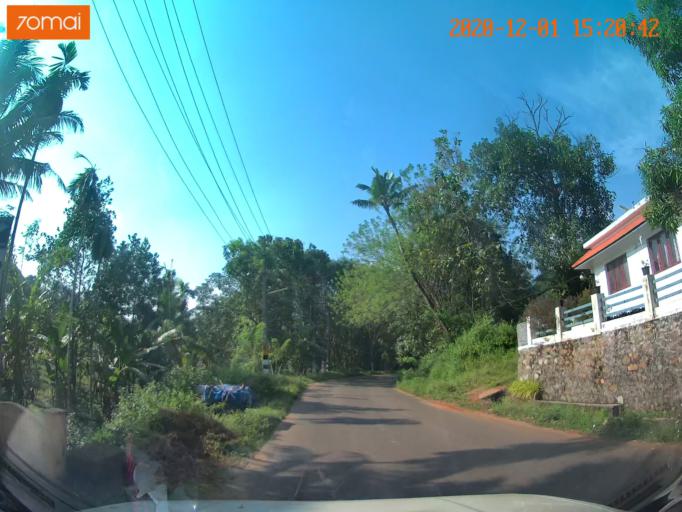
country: IN
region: Kerala
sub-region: Ernakulam
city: Ramamangalam
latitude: 9.9442
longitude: 76.5393
